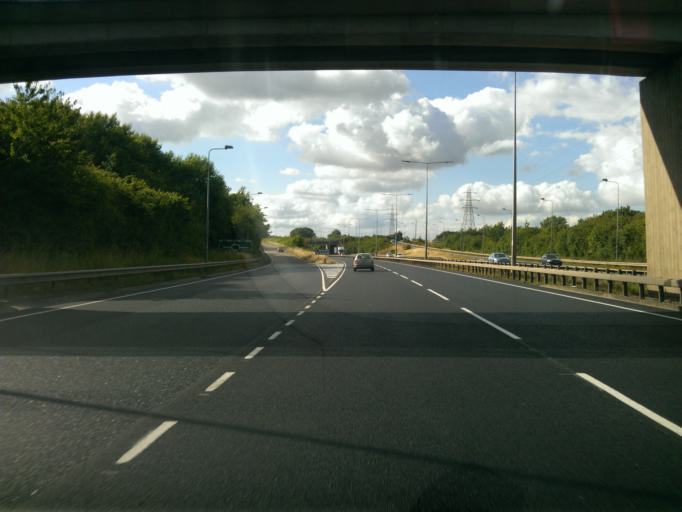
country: GB
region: England
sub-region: Staffordshire
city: Fazeley
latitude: 52.6177
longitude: -1.6673
